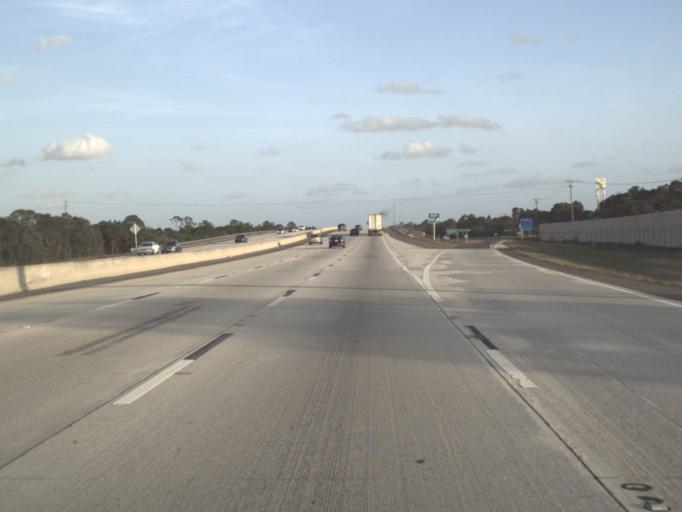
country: US
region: Florida
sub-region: Brevard County
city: Cocoa West
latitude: 28.3779
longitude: -80.8067
